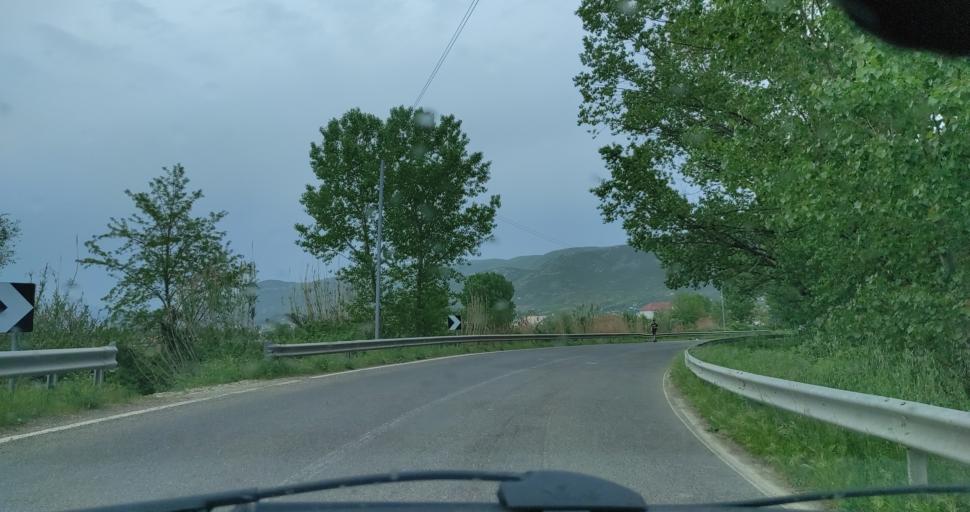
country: AL
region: Lezhe
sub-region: Rrethi i Kurbinit
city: Mamurras
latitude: 41.6004
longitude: 19.6999
